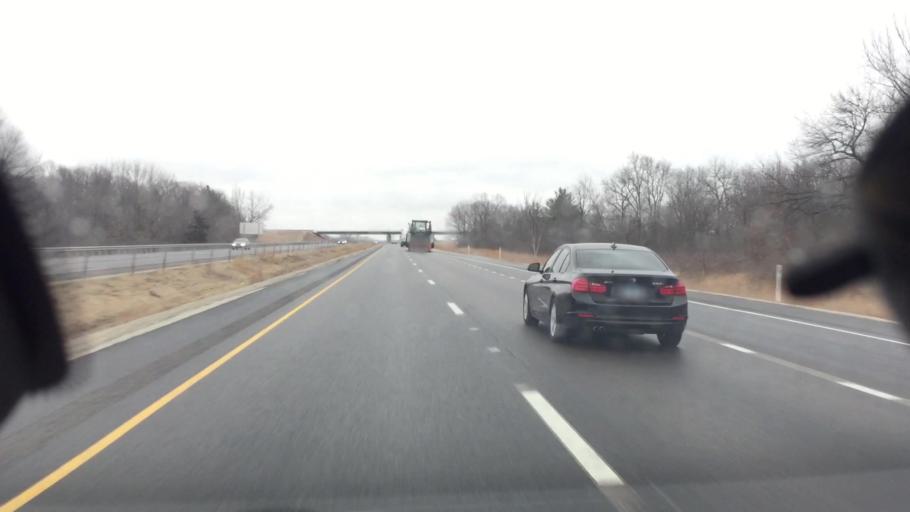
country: US
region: Illinois
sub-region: Tazewell County
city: East Peoria
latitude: 40.6386
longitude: -89.5297
